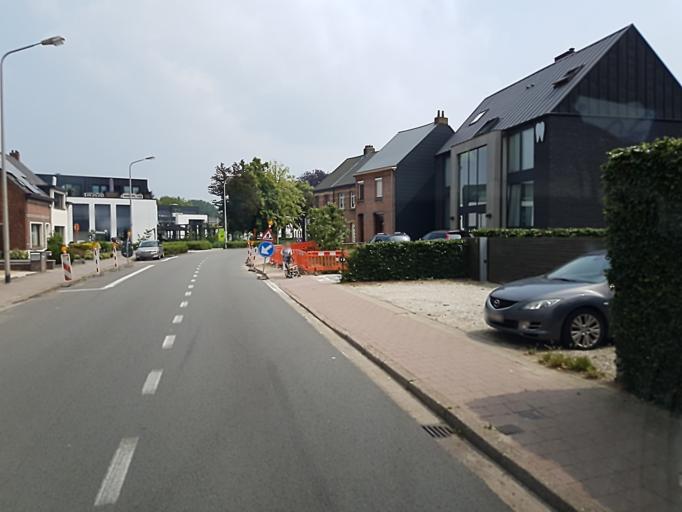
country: BE
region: Flanders
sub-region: Provincie Antwerpen
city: Nijlen
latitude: 51.1630
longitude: 4.6664
